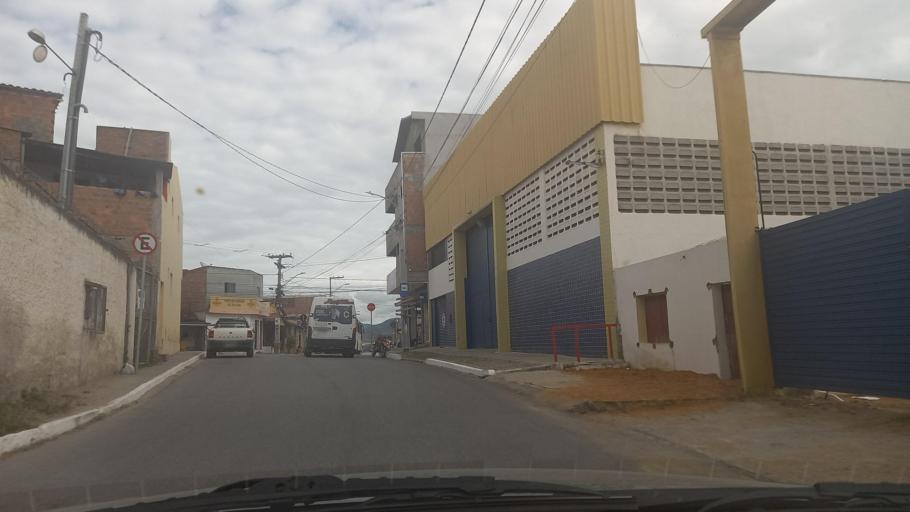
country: BR
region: Pernambuco
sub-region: Caruaru
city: Caruaru
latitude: -8.2912
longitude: -36.0304
